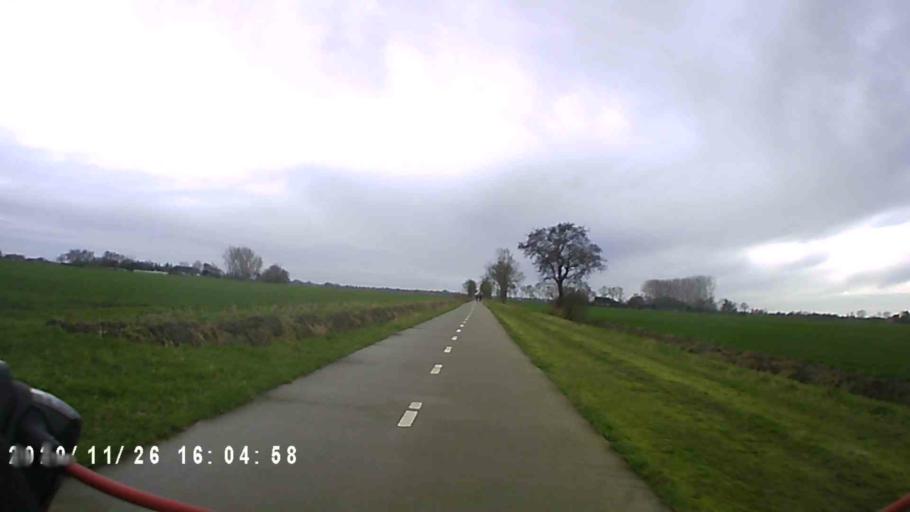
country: NL
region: Groningen
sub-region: Gemeente Bedum
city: Bedum
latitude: 53.2679
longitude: 6.6765
